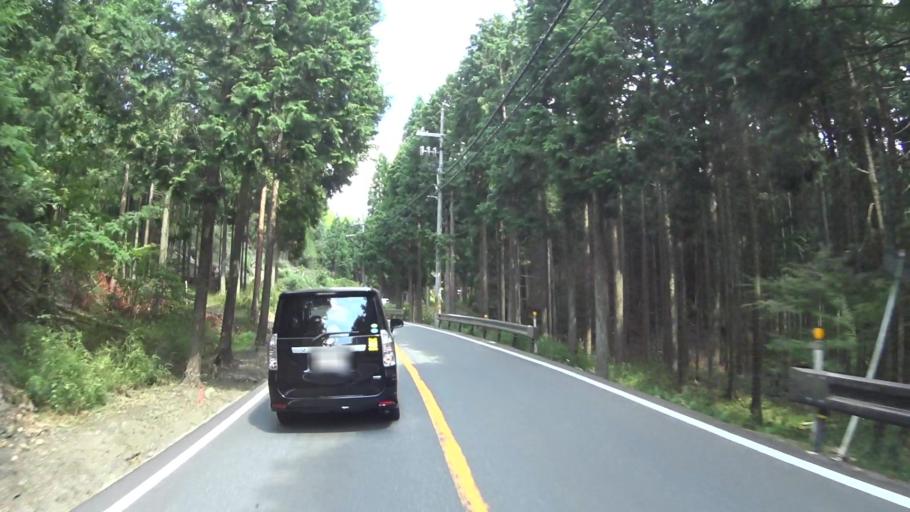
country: JP
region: Kyoto
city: Kameoka
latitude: 35.2766
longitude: 135.5690
